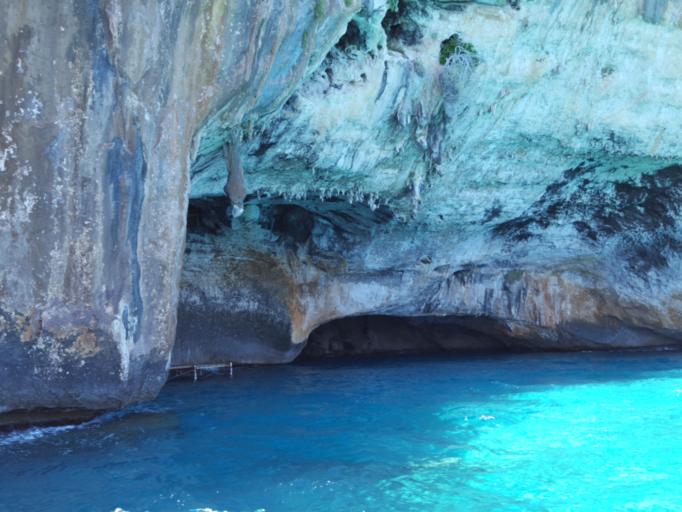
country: IT
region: Sardinia
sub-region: Provincia di Nuoro
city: Cala Gonone
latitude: 40.2466
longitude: 9.6232
